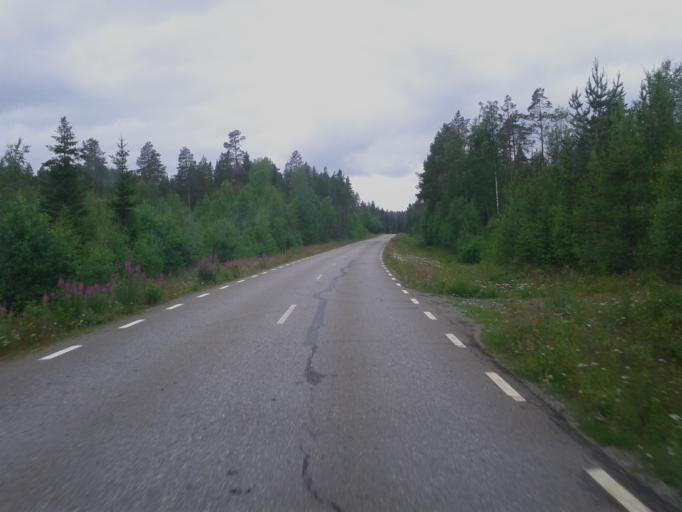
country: SE
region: Vaesterbotten
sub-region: Skelleftea Kommun
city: Kage
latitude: 64.9178
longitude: 20.9091
